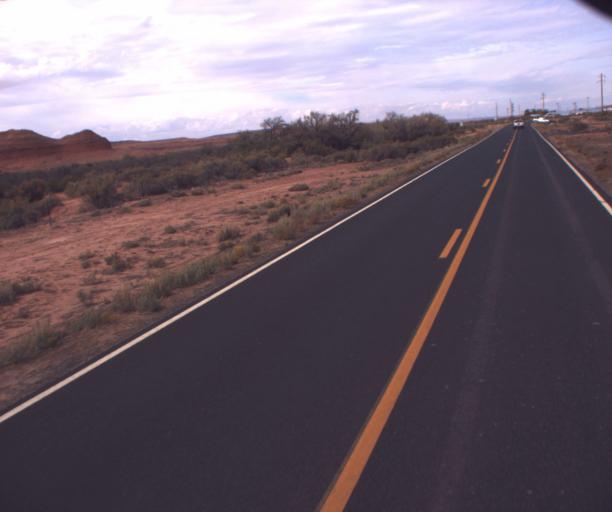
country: US
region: Arizona
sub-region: Apache County
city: Many Farms
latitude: 36.7119
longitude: -109.6241
